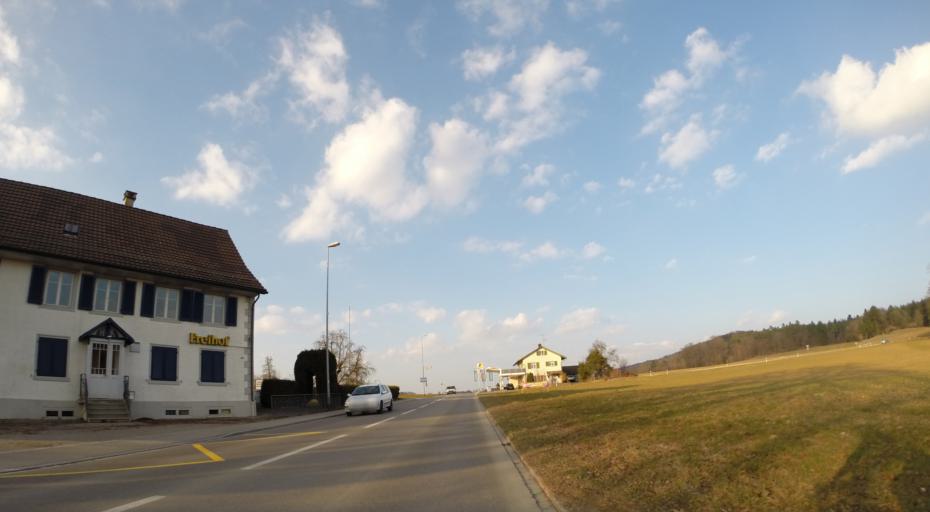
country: CH
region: Thurgau
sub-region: Frauenfeld District
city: Steckborn
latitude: 47.6367
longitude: 8.9741
